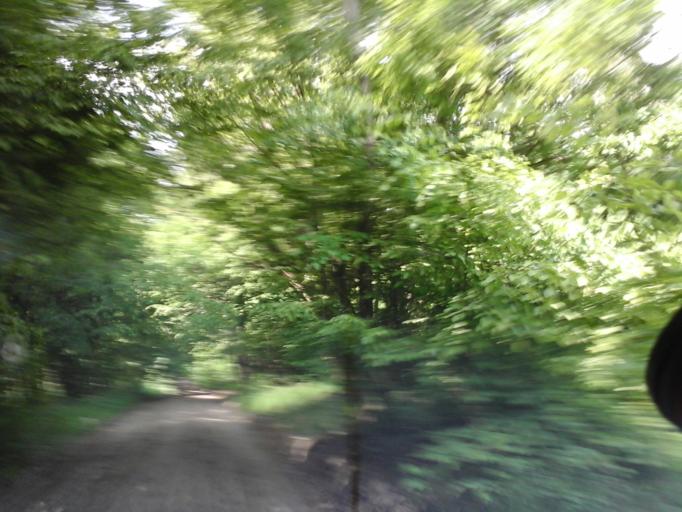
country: PL
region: West Pomeranian Voivodeship
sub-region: Powiat choszczenski
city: Drawno
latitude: 53.1392
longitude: 15.8330
